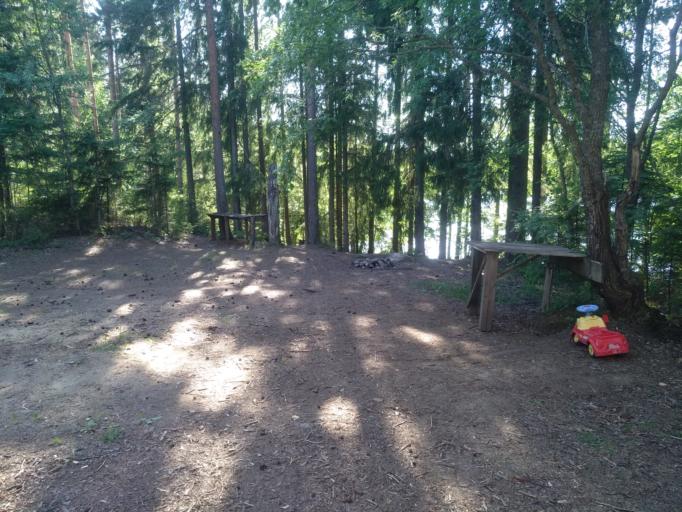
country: RU
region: Leningrad
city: Yakovlevo
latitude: 60.3507
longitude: 29.3394
